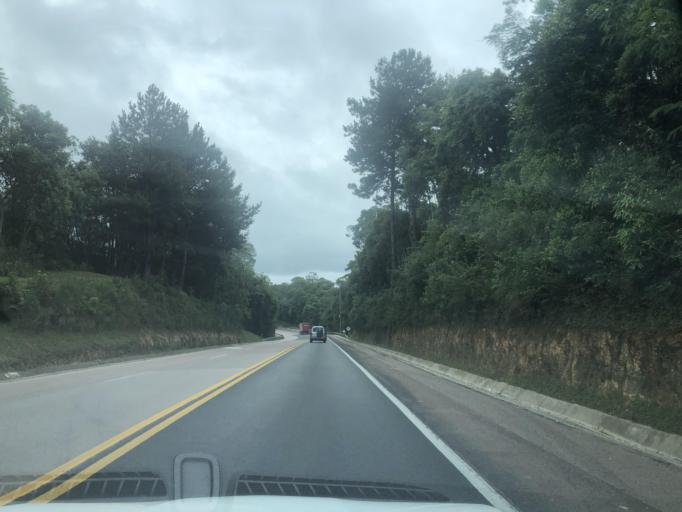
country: BR
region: Parana
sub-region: Araucaria
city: Araucaria
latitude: -25.8199
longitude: -49.3338
